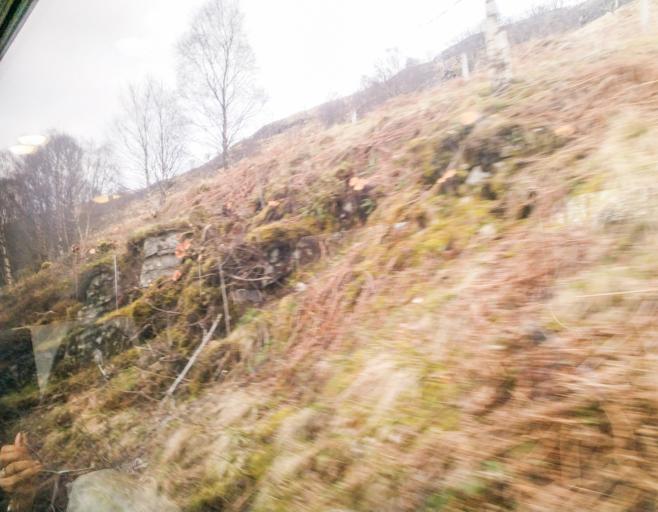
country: GB
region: Scotland
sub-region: Highland
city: Spean Bridge
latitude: 56.7893
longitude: -4.7285
